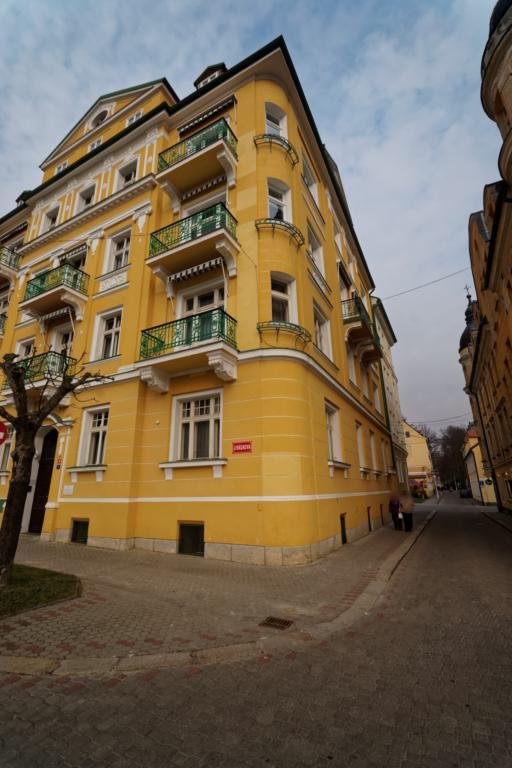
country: CZ
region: Karlovarsky
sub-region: Okres Cheb
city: Frantiskovy Lazne
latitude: 50.1180
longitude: 12.3517
